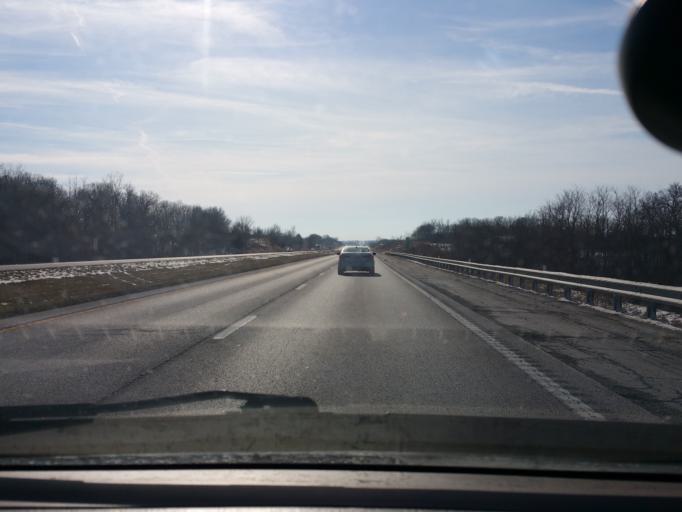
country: US
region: Missouri
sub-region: Clinton County
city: Cameron
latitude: 39.7058
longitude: -94.2263
